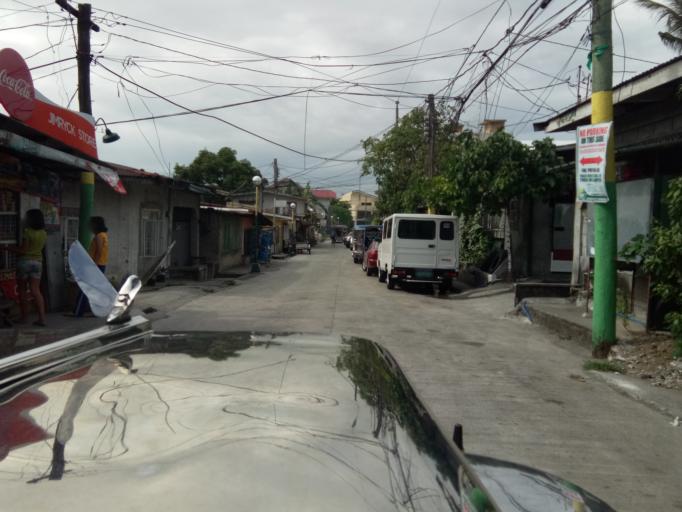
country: PH
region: Calabarzon
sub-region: Province of Cavite
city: Dasmarinas
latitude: 14.3271
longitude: 120.9380
